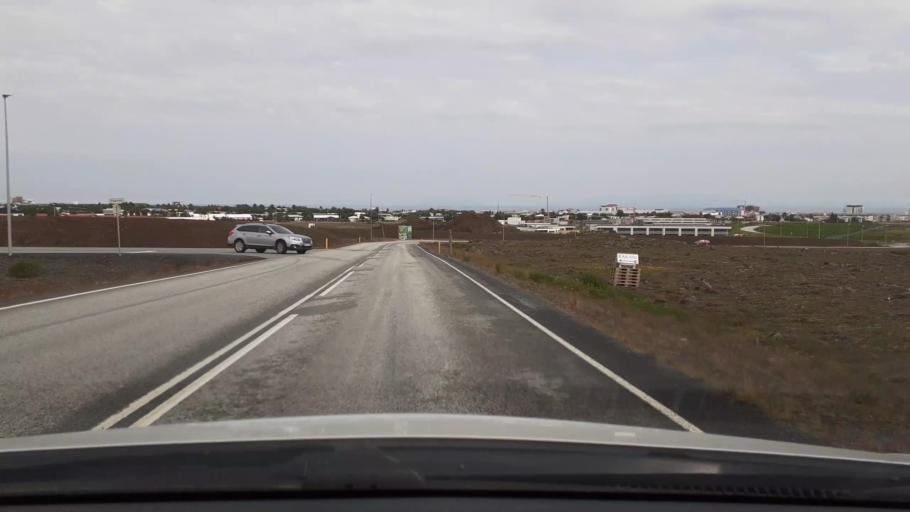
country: IS
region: Southern Peninsula
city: Reykjanesbaer
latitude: 63.9921
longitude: -22.5755
